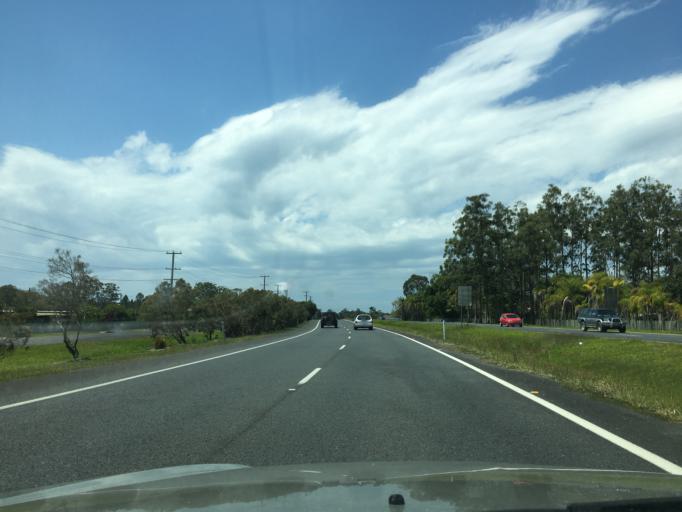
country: AU
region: Queensland
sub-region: Moreton Bay
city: Caboolture
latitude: -27.0744
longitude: 153.0546
